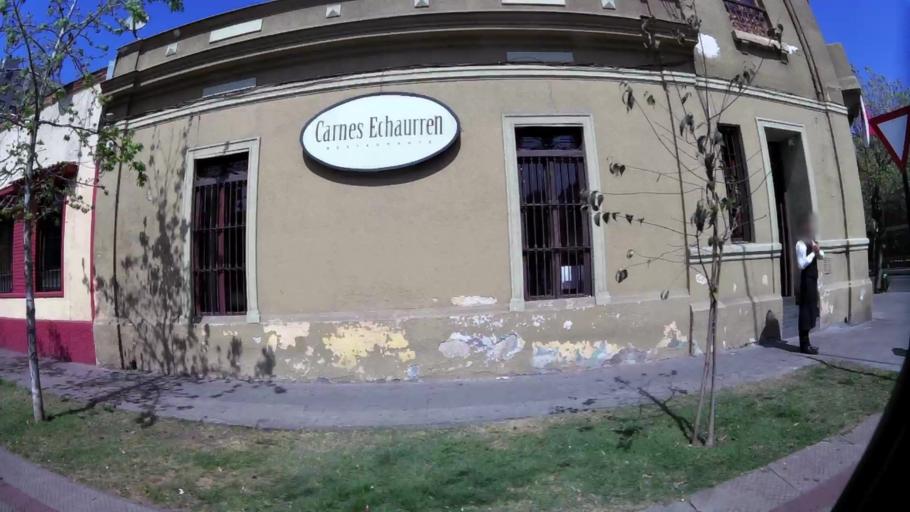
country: CL
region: Santiago Metropolitan
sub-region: Provincia de Santiago
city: Santiago
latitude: -33.4532
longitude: -70.6662
